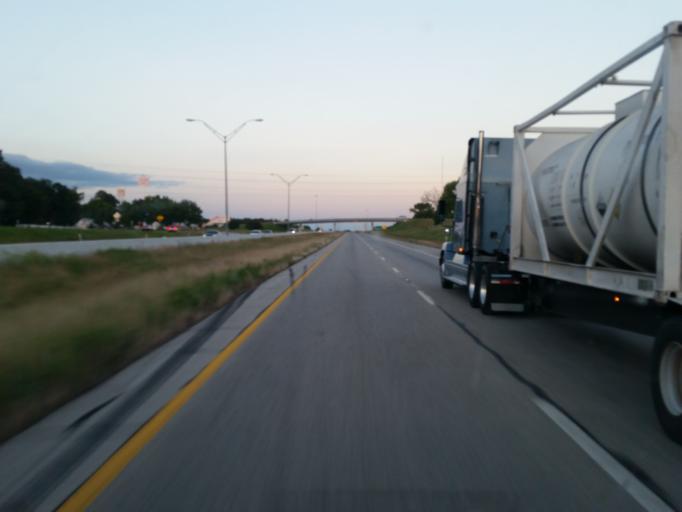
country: US
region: Texas
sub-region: Smith County
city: Hideaway
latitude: 32.4700
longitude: -95.4566
